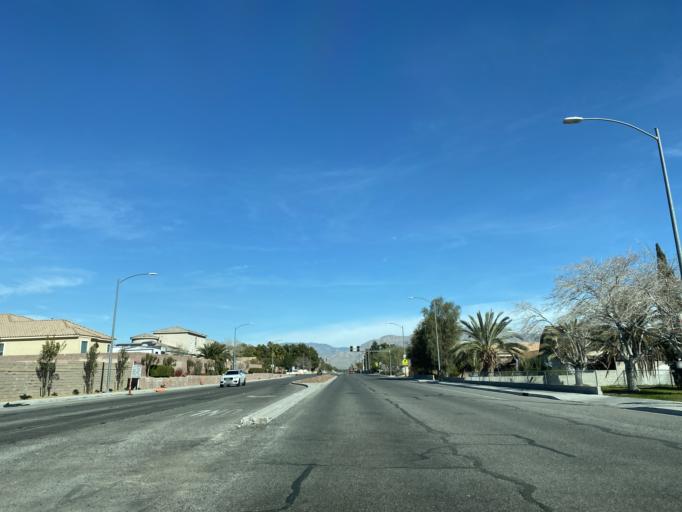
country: US
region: Nevada
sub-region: Clark County
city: Las Vegas
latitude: 36.2519
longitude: -115.2255
